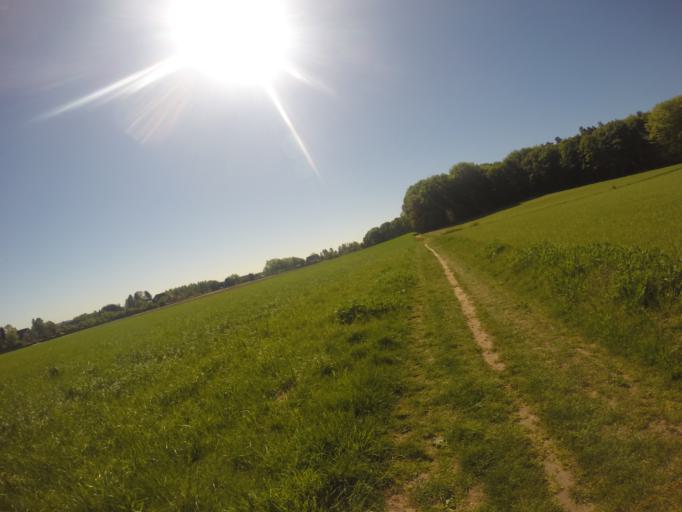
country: NL
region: Gelderland
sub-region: Gemeente Montferland
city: s-Heerenberg
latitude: 51.9233
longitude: 6.2463
